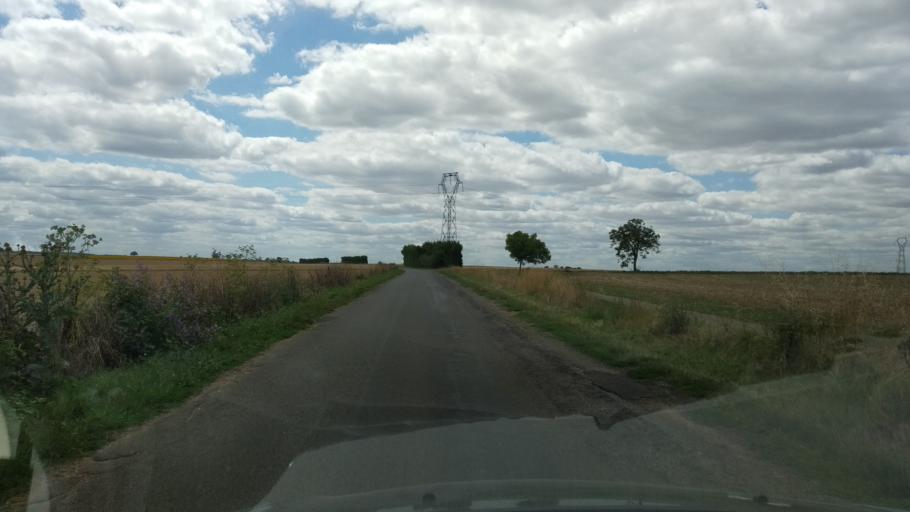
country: FR
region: Poitou-Charentes
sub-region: Departement de la Vienne
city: Jaunay-Clan
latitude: 46.6779
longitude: 0.3477
